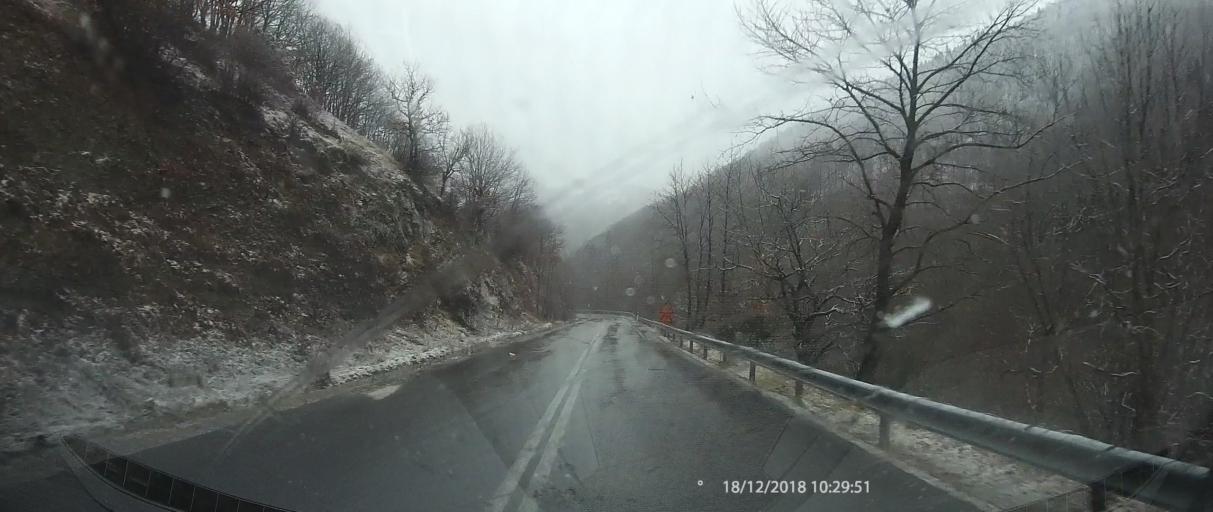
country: GR
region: Central Macedonia
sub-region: Nomos Pierias
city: Kato Milia
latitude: 40.1850
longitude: 22.2744
